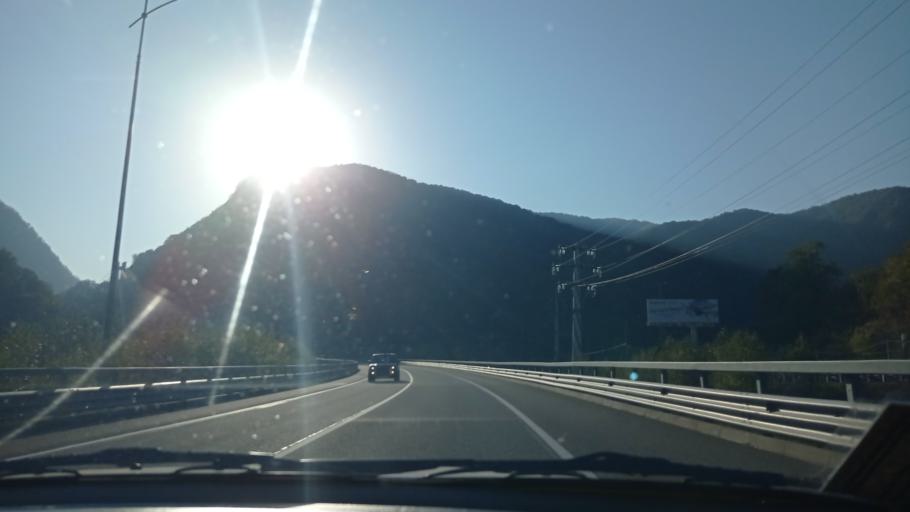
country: RU
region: Krasnodarskiy
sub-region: Sochi City
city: Krasnaya Polyana
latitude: 43.6157
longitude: 40.0552
